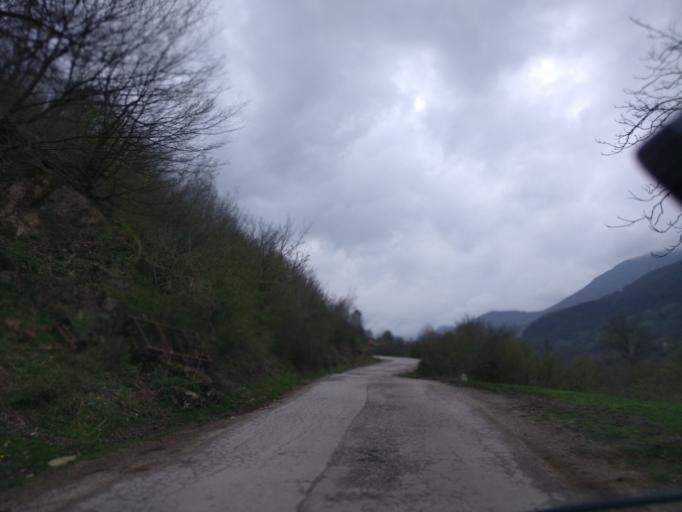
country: BA
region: Republika Srpska
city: Foca
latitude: 43.4396
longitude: 18.7628
